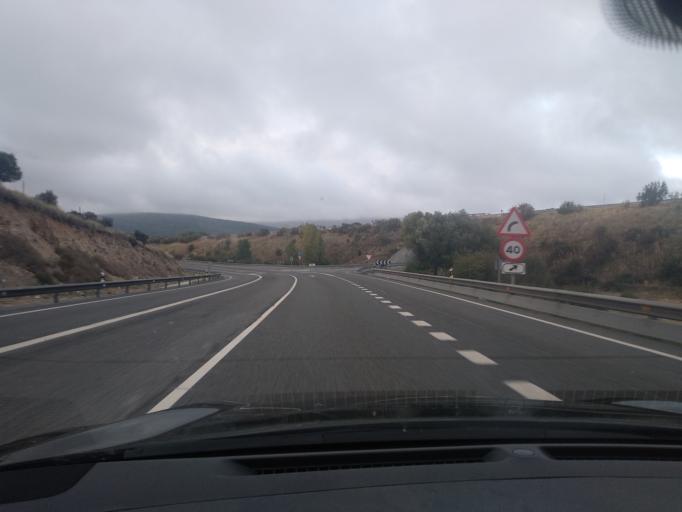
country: ES
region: Castille and Leon
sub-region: Provincia de Segovia
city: Otero de Herreros
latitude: 40.7593
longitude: -4.2111
